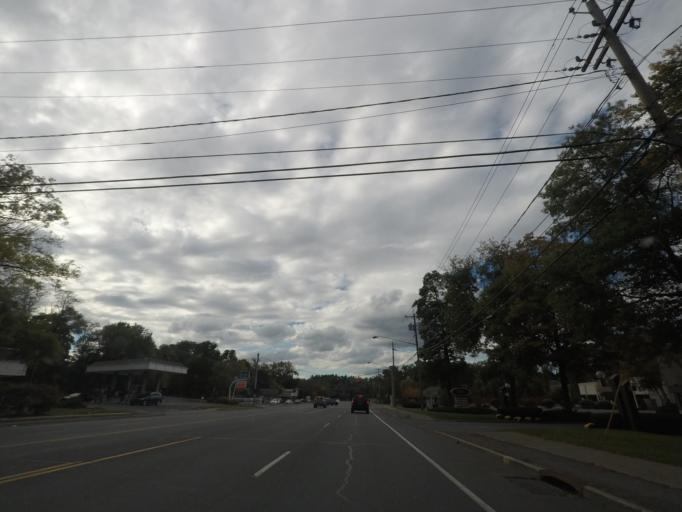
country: US
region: New York
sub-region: Albany County
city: Westmere
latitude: 42.6924
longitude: -73.8731
